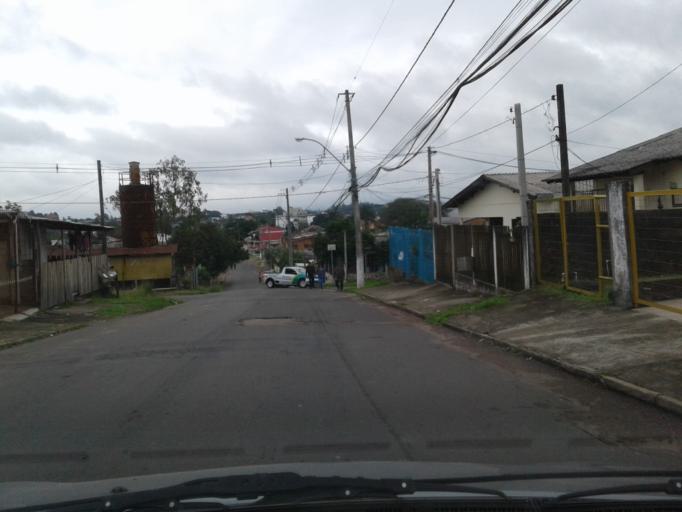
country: BR
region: Rio Grande do Sul
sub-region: Gravatai
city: Gravatai
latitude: -29.9339
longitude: -51.0154
